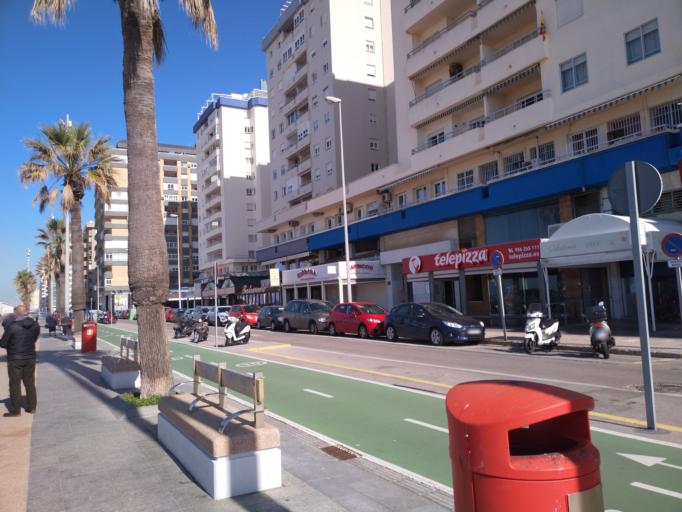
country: ES
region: Andalusia
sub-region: Provincia de Cadiz
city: Cadiz
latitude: 36.5067
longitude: -6.2789
